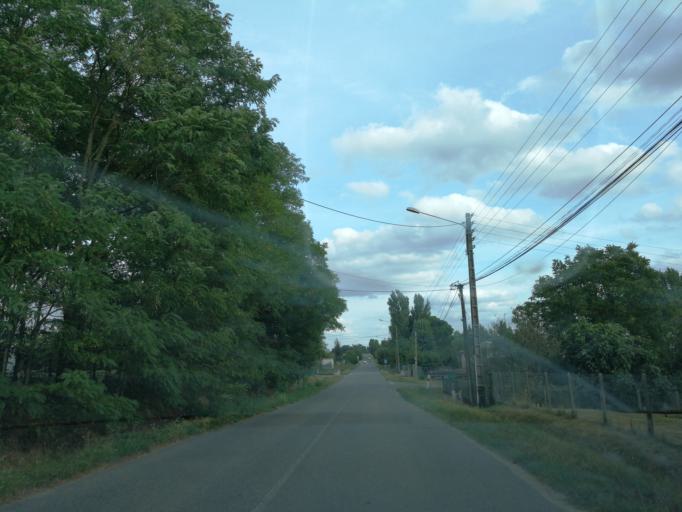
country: FR
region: Midi-Pyrenees
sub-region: Departement de la Haute-Garonne
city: Flourens
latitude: 43.6000
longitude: 1.5447
